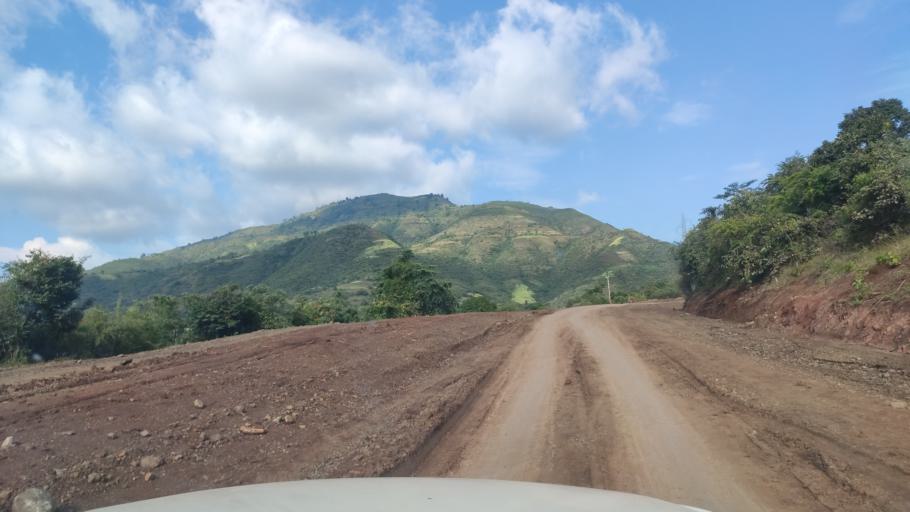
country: ET
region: Southern Nations, Nationalities, and People's Region
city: Arba Minch'
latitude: 6.4256
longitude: 37.3383
